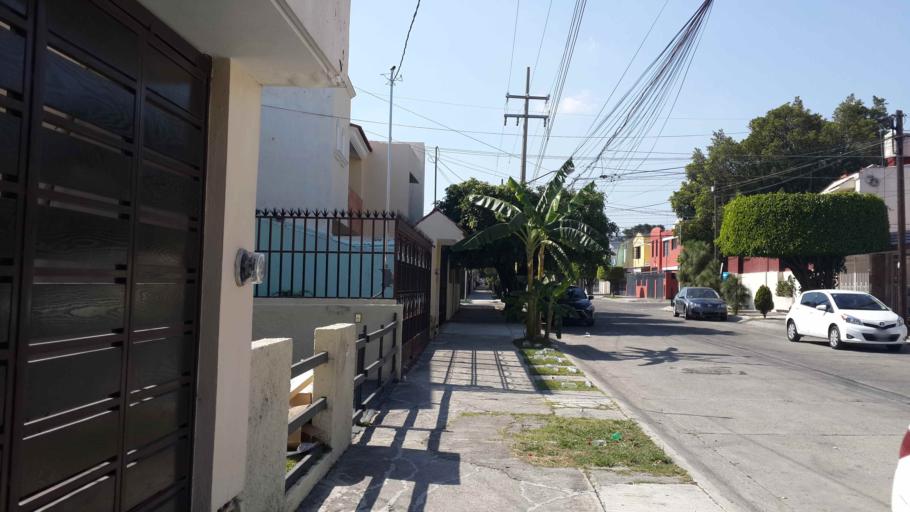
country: MX
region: Jalisco
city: Guadalajara
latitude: 20.6680
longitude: -103.4290
